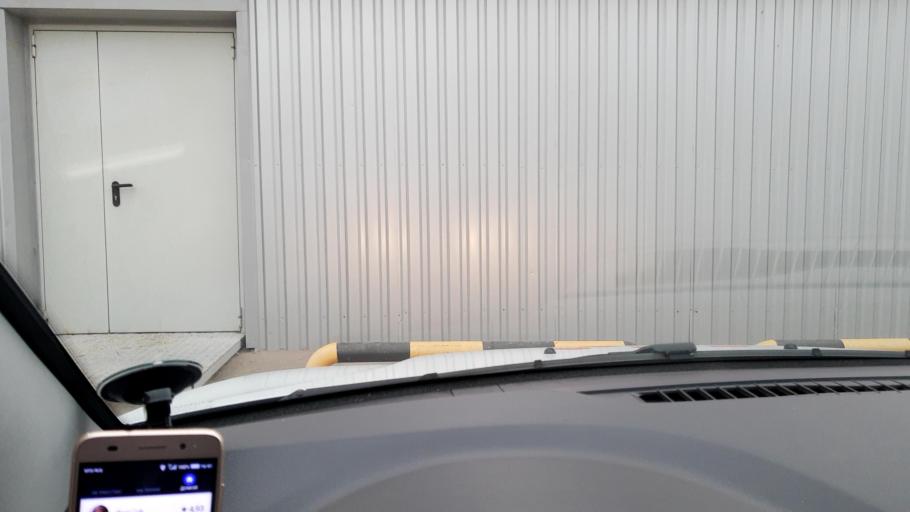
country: RU
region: Nizjnij Novgorod
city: Nizhniy Novgorod
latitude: 56.2905
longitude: 43.9025
